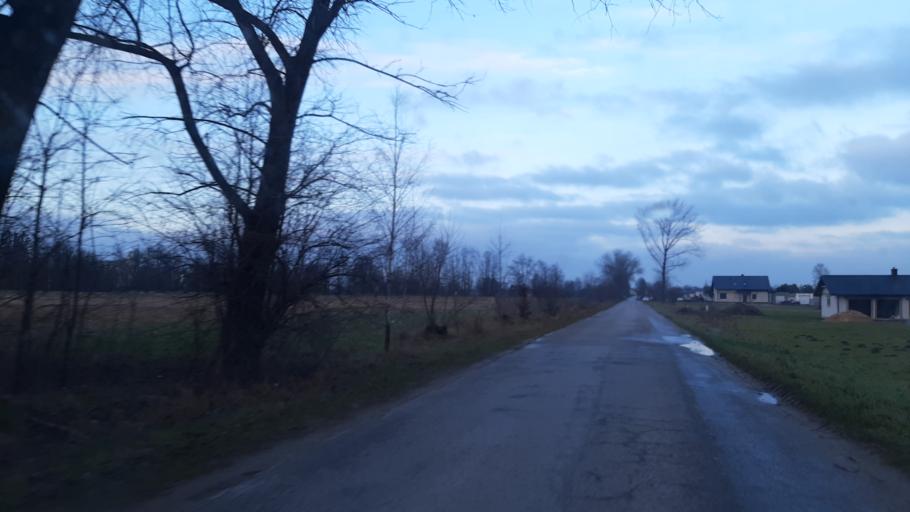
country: PL
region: Lublin Voivodeship
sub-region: Powiat lubelski
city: Garbow
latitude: 51.3964
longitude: 22.4099
